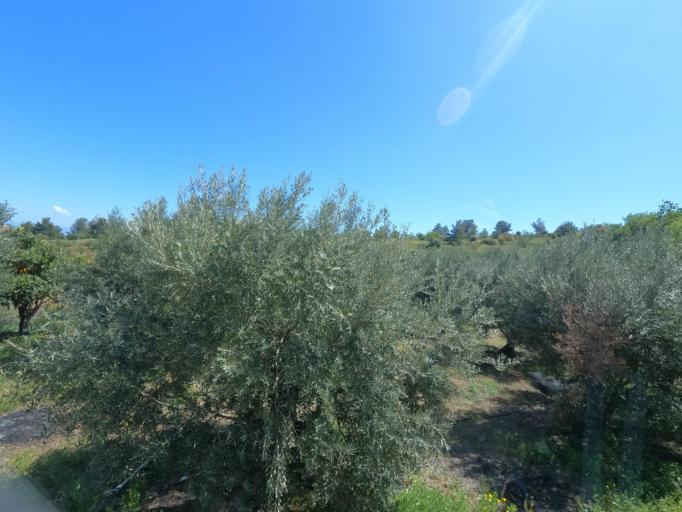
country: CY
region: Lefkosia
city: Peristerona
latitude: 35.0455
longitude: 33.0648
